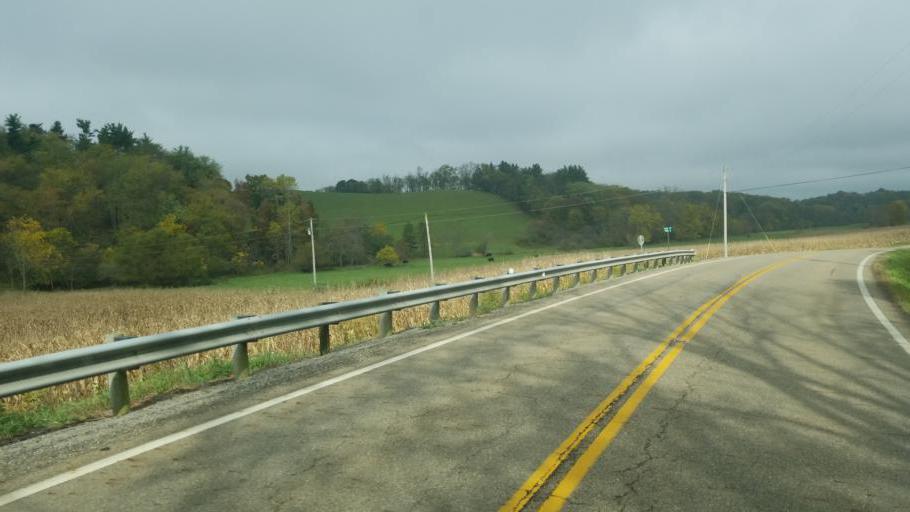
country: US
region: Ohio
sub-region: Carroll County
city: Lake Mohawk
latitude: 40.5752
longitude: -81.2569
